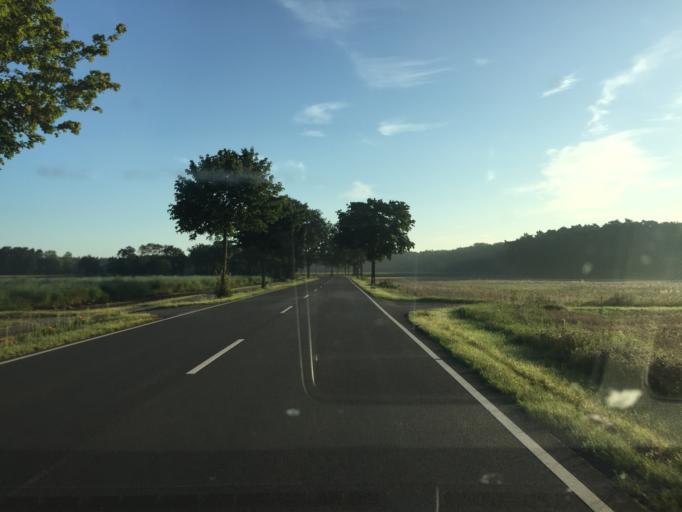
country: DE
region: Lower Saxony
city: Heemsen
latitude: 52.7271
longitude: 9.2909
